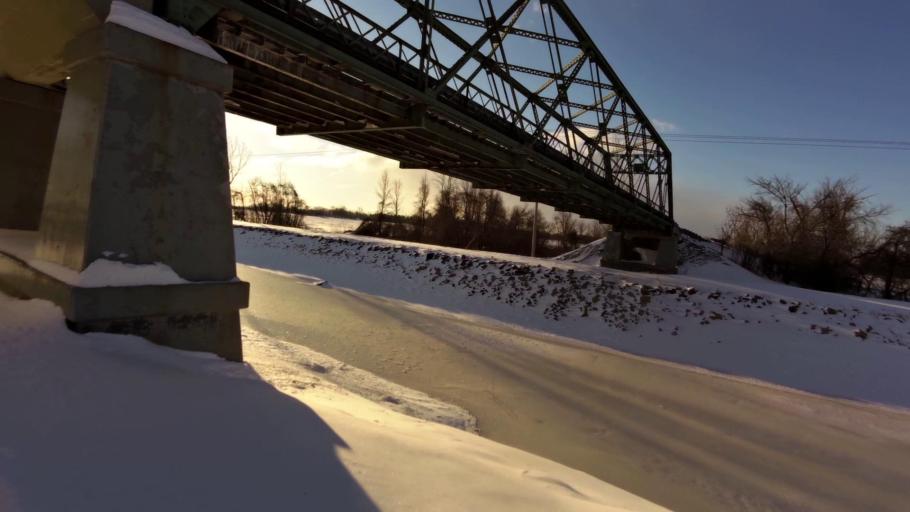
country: US
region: New York
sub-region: Orleans County
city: Medina
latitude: 43.2339
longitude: -78.3557
